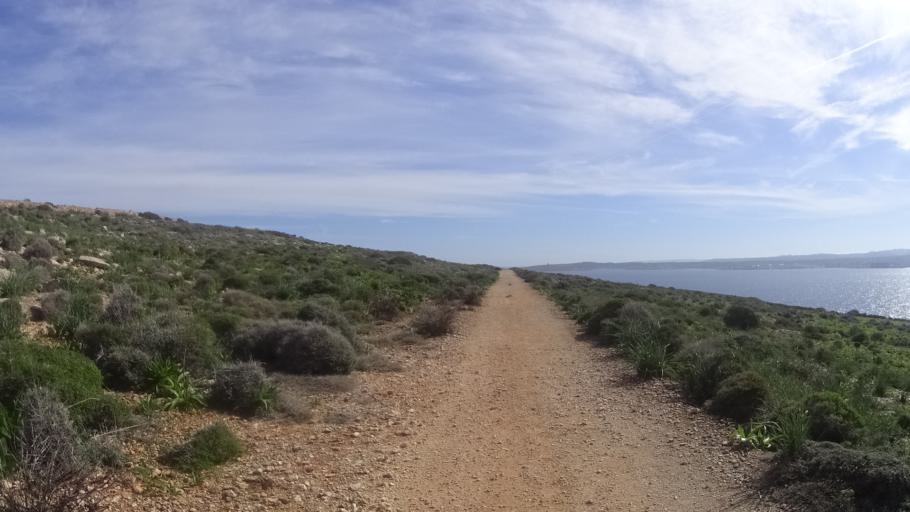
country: MT
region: Il-Qala
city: Qala
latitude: 36.0071
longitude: 14.3349
